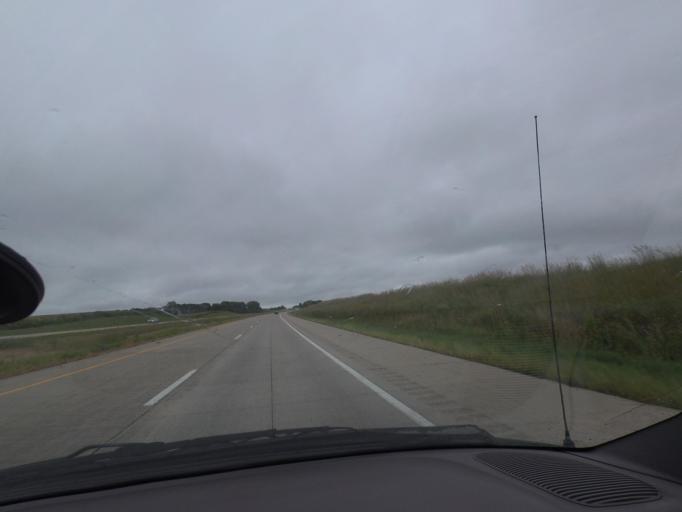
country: US
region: Illinois
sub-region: Sangamon County
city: Riverton
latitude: 39.8394
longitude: -89.4603
